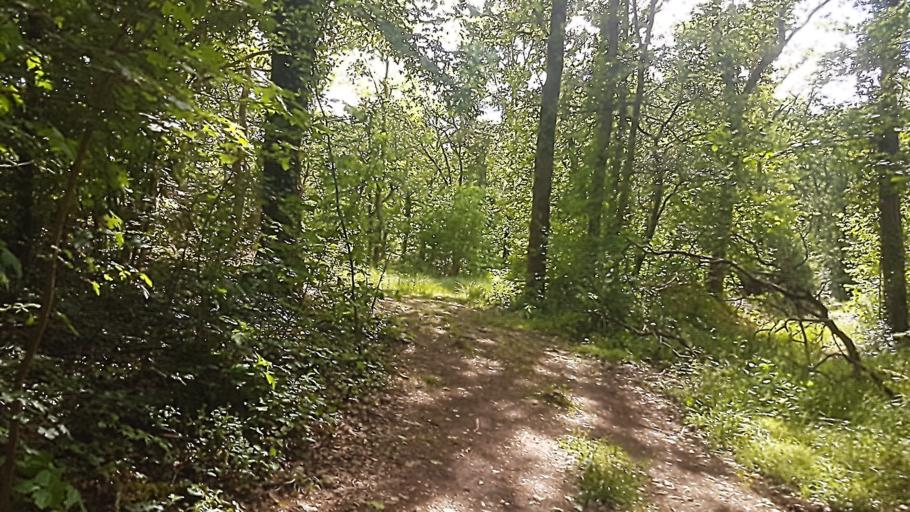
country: BE
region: Wallonia
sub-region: Province de Namur
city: Couvin
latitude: 50.0778
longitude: 4.5943
